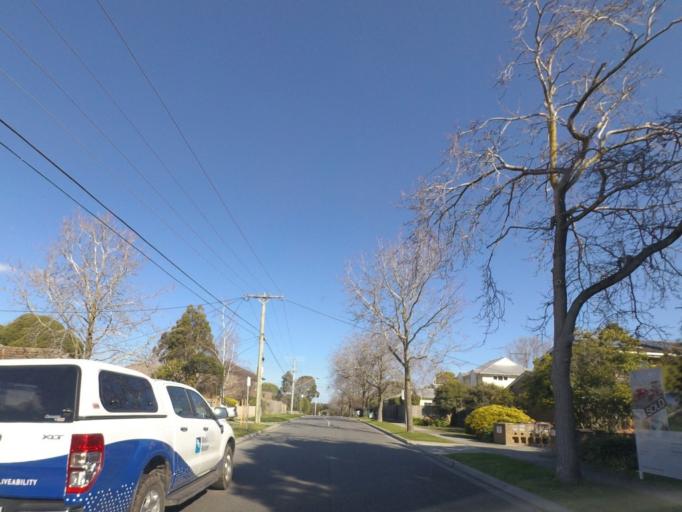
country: AU
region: Victoria
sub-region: Maroondah
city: Ringwood East
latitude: -37.8188
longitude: 145.2342
